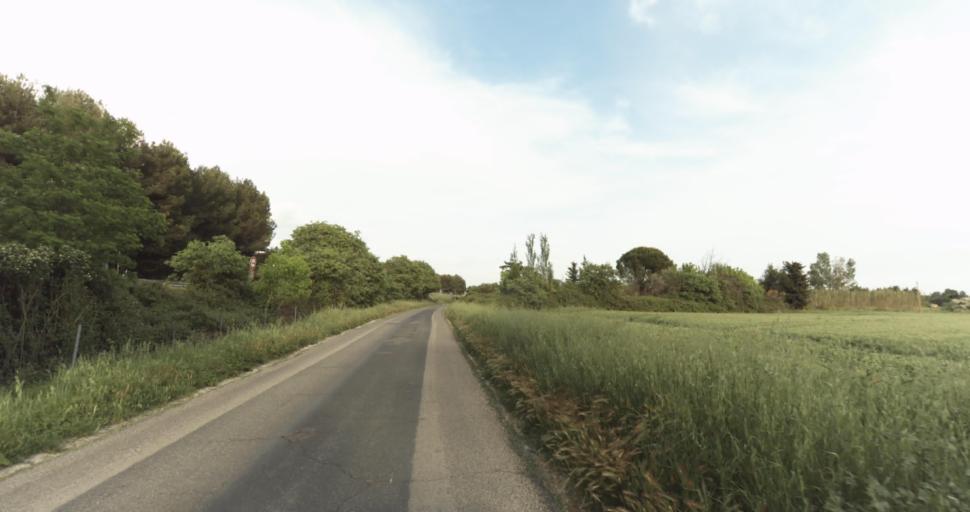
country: FR
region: Languedoc-Roussillon
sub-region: Departement du Gard
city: Nimes
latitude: 43.8092
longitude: 4.3447
